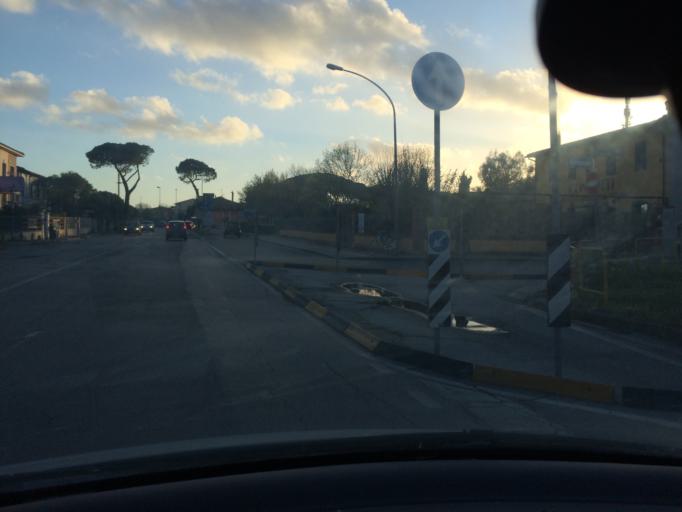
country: IT
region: Tuscany
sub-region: Province of Pisa
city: Pisa
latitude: 43.7216
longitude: 10.4231
